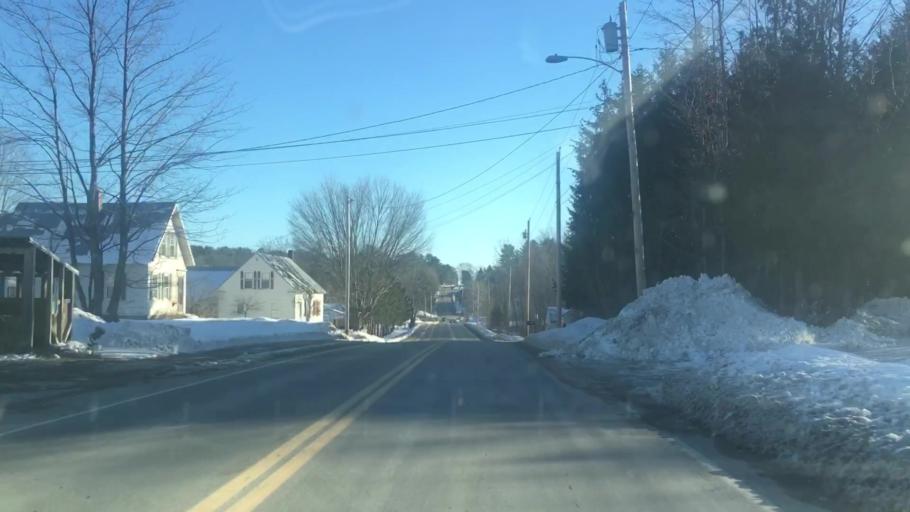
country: US
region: Maine
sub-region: Somerset County
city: Norridgewock
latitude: 44.7128
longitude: -69.7962
